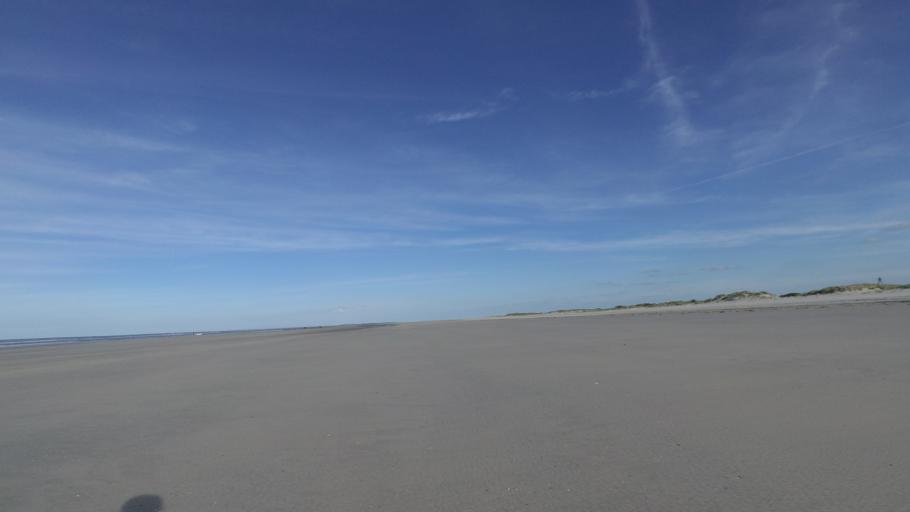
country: NL
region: Friesland
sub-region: Gemeente Dongeradeel
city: Ternaard
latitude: 53.4680
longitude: 5.9228
